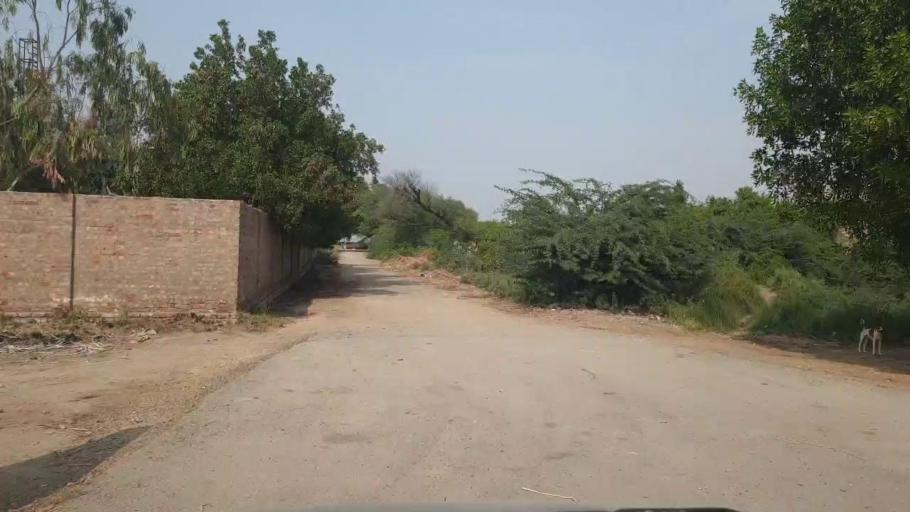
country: PK
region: Sindh
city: Tando Muhammad Khan
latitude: 25.1316
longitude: 68.4208
